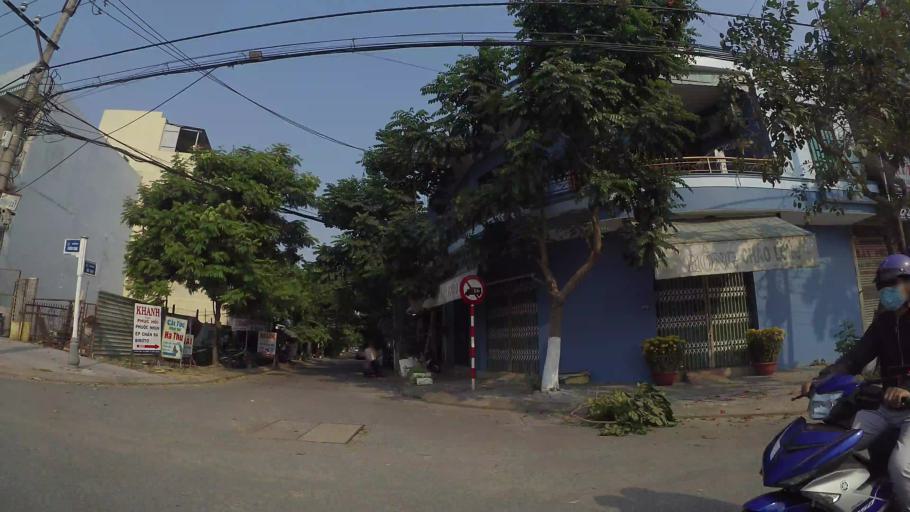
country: VN
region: Da Nang
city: Cam Le
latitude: 16.0191
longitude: 108.1939
